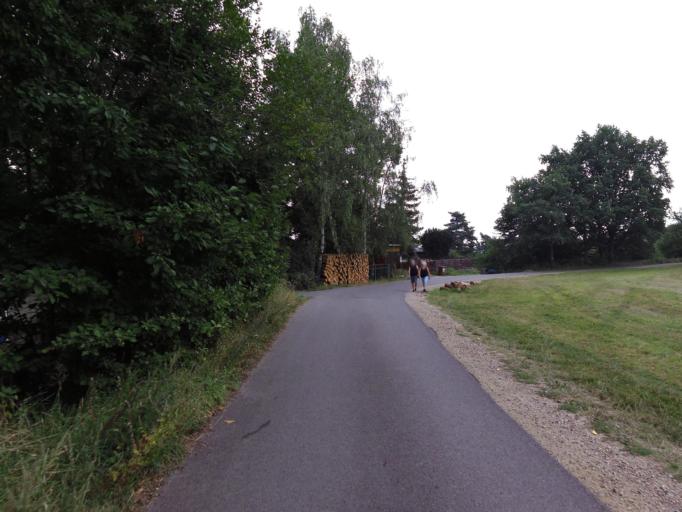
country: CZ
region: Central Bohemia
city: Kamenice
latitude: 49.8902
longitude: 14.6137
